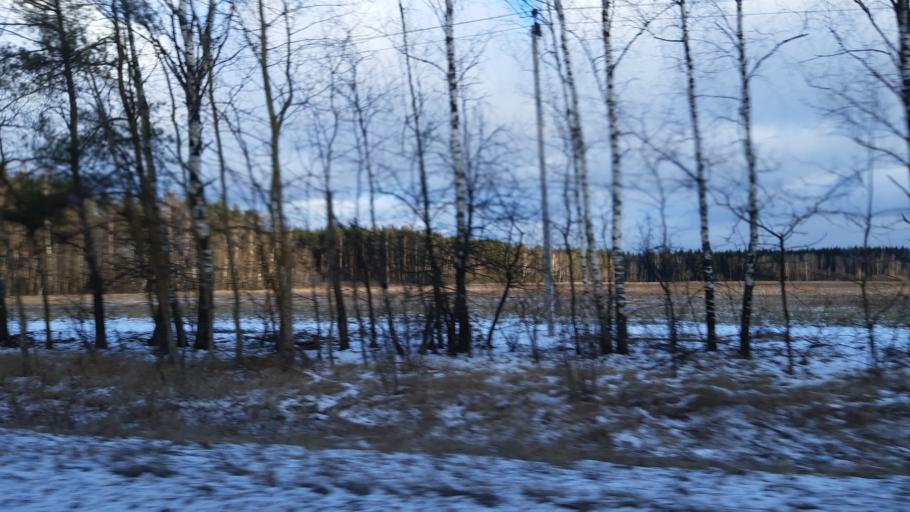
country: RU
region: Moskovskaya
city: Noginsk-9
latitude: 56.0443
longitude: 38.5523
